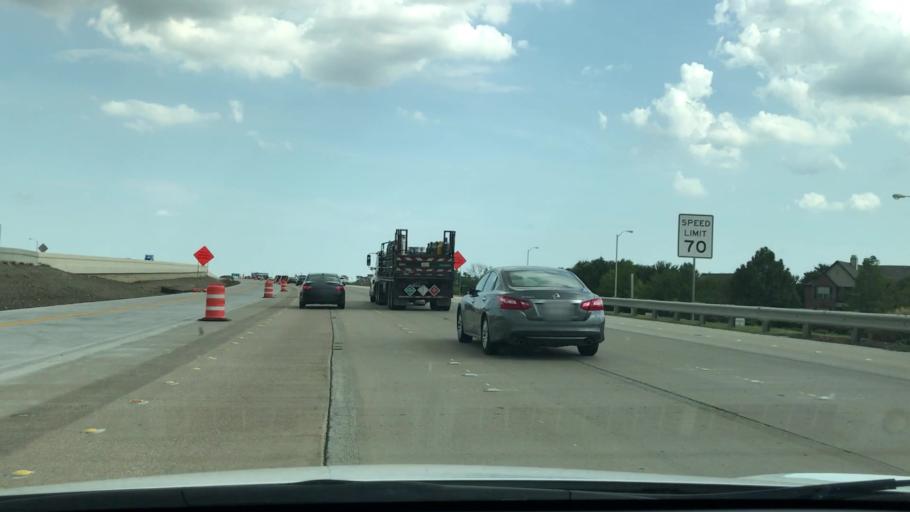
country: US
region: Texas
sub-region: Collin County
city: Plano
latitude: 32.9775
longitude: -96.6609
